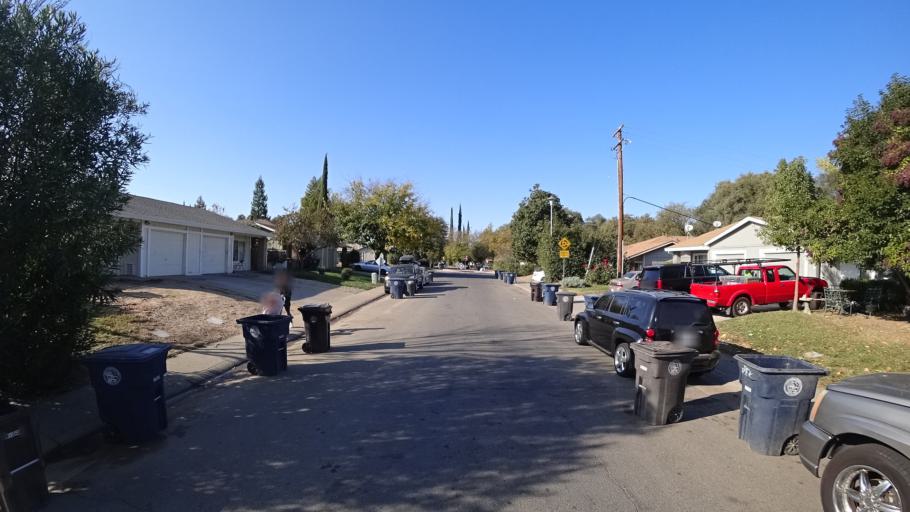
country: US
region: California
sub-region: Sacramento County
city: Citrus Heights
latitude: 38.6839
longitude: -121.2775
